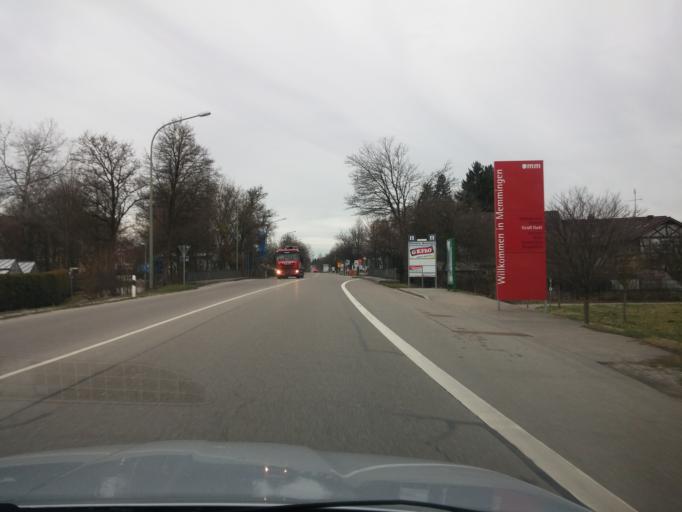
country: DE
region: Bavaria
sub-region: Swabia
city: Trunkelsberg
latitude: 47.9976
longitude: 10.2005
